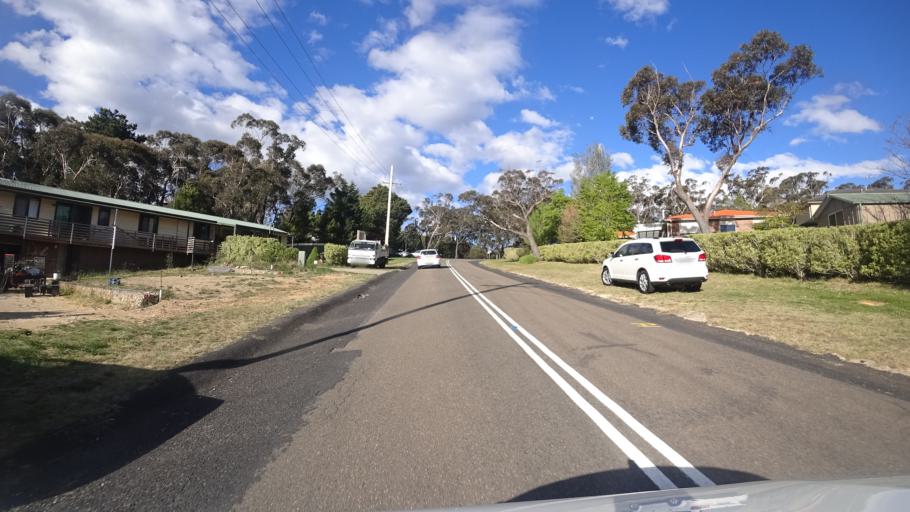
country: AU
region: New South Wales
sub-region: Blue Mountains Municipality
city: Katoomba
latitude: -33.7205
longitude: 150.2927
